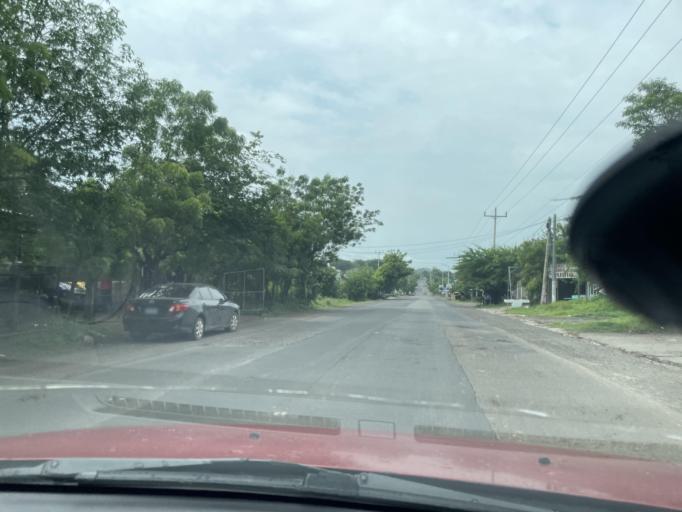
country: SV
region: La Union
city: Santa Rosa de Lima
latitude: 13.6245
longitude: -87.8683
